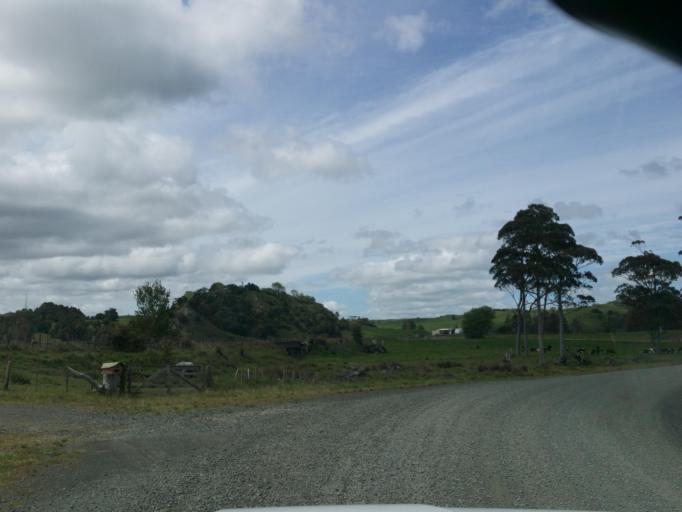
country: NZ
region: Northland
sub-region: Kaipara District
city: Dargaville
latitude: -35.8690
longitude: 174.0353
